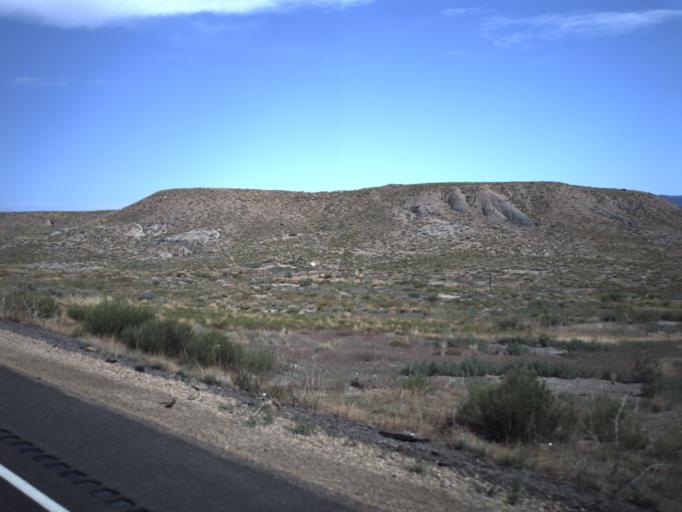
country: US
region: Utah
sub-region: Carbon County
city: East Carbon City
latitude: 39.4726
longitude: -110.5009
